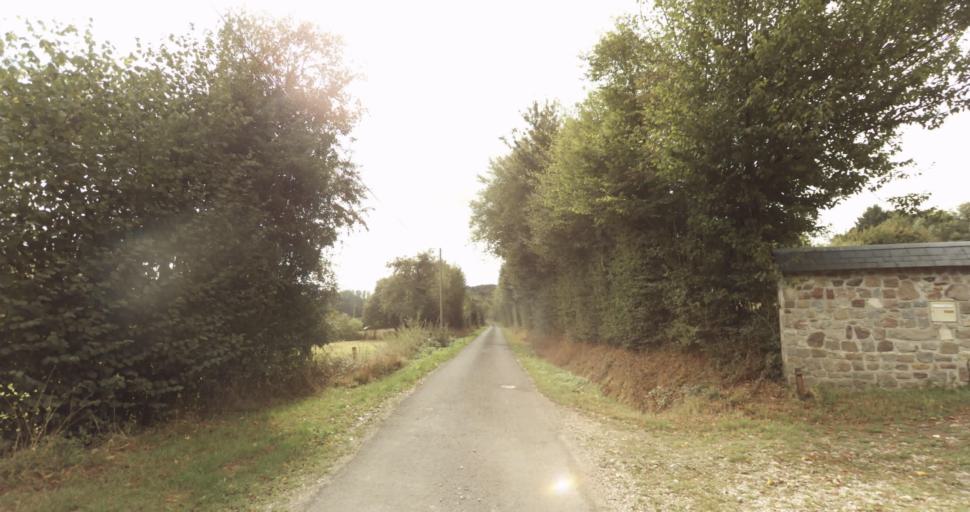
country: FR
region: Lower Normandy
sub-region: Departement de l'Orne
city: Gace
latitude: 48.8480
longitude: 0.2849
